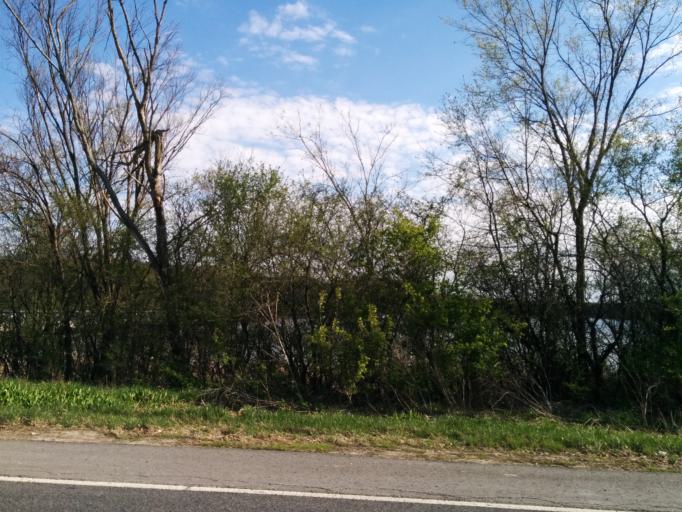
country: US
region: Illinois
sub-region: Cook County
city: Willow Springs
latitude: 41.7173
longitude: -87.8765
